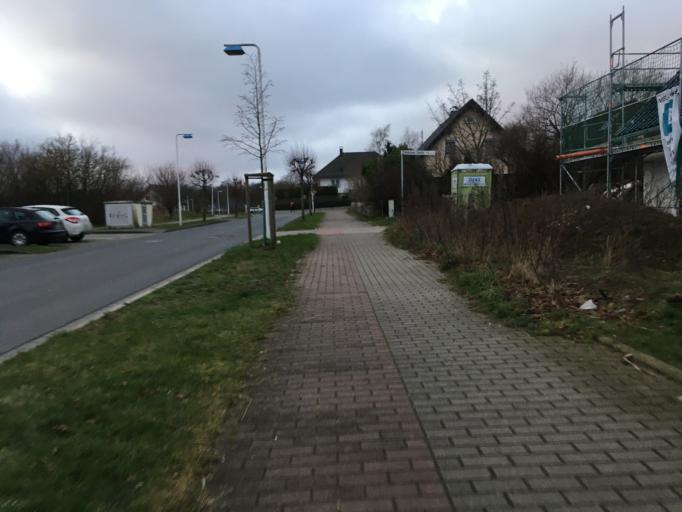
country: DE
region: Mecklenburg-Vorpommern
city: Sassnitz
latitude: 54.5120
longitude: 13.6079
